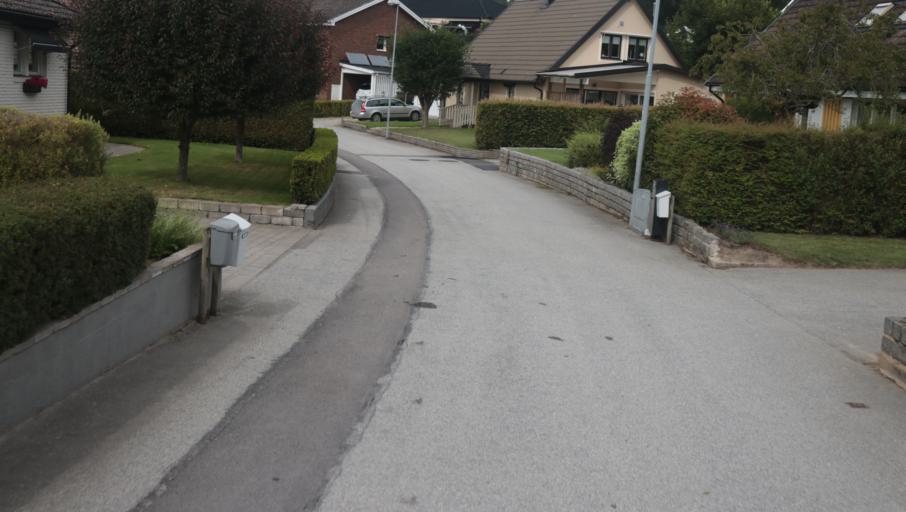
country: SE
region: Blekinge
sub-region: Karlshamns Kommun
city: Karlshamn
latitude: 56.2070
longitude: 14.8542
